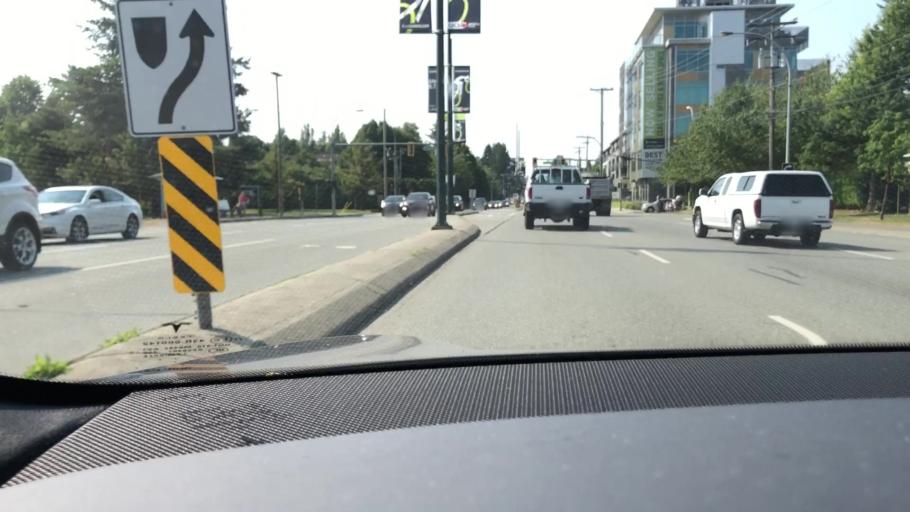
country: US
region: Washington
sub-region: Whatcom County
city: Point Roberts
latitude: 49.0360
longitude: -123.0687
